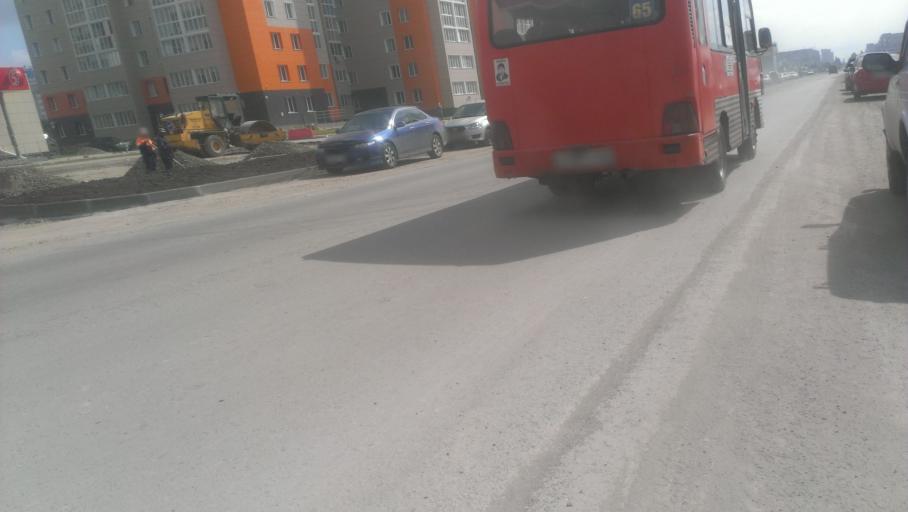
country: RU
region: Altai Krai
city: Novosilikatnyy
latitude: 53.3375
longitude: 83.6541
